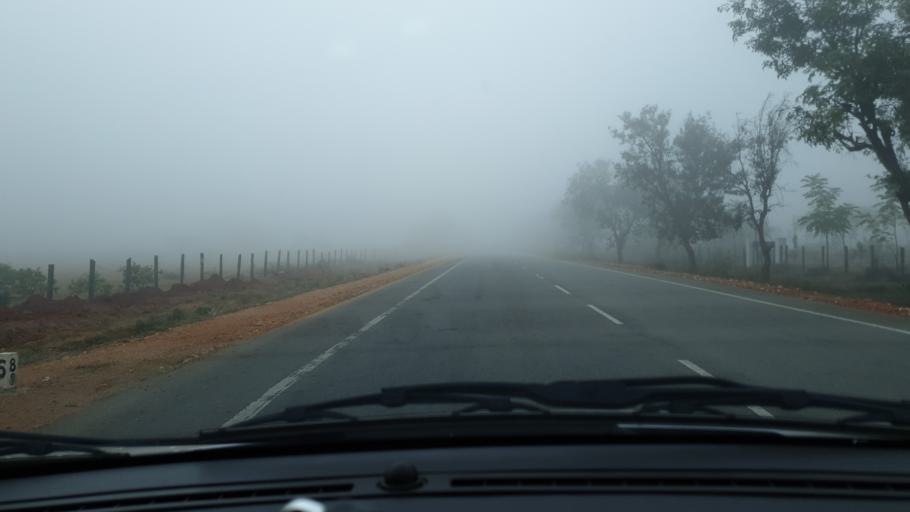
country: IN
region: Telangana
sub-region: Mahbubnagar
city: Nagar Karnul
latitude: 16.6492
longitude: 78.5785
